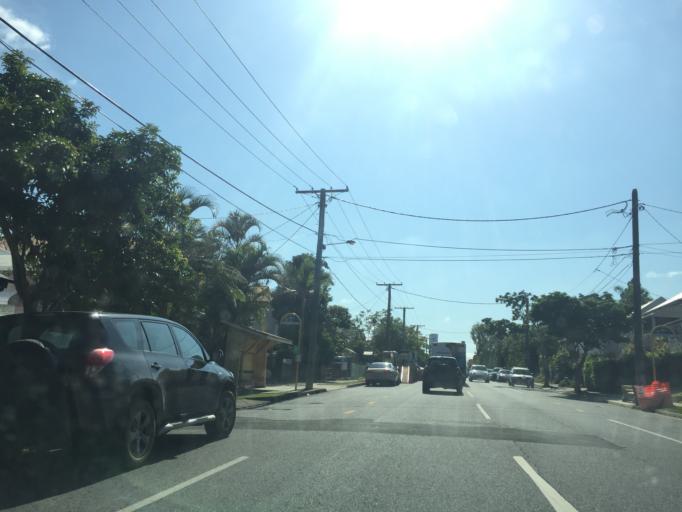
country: AU
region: Queensland
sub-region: Brisbane
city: Milton
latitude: -27.4646
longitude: 152.9931
